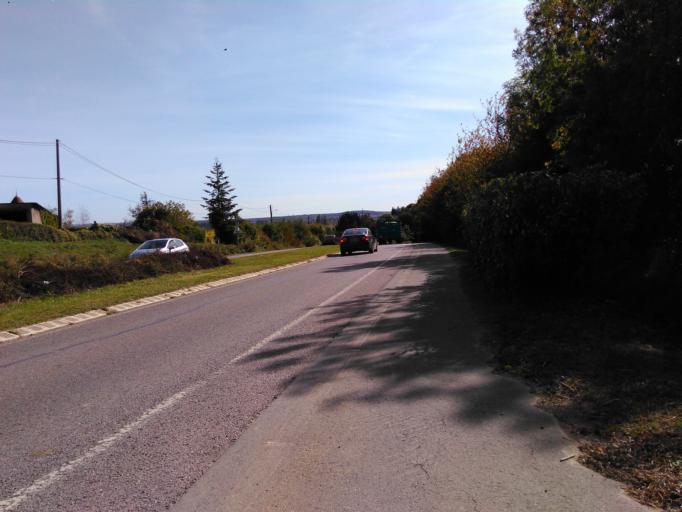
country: FR
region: Lorraine
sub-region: Departement de la Moselle
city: Thionville
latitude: 49.3841
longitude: 6.1685
